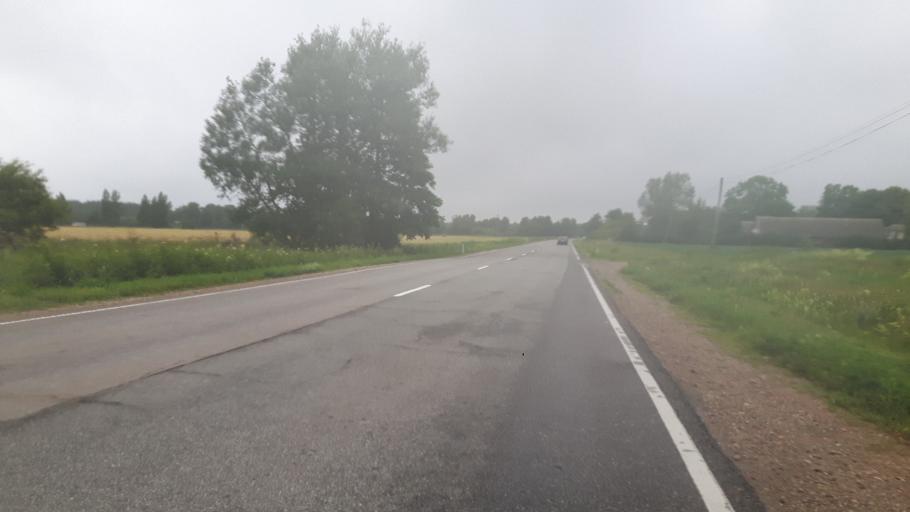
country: LV
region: Nica
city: Nica
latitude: 56.4076
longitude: 21.0039
